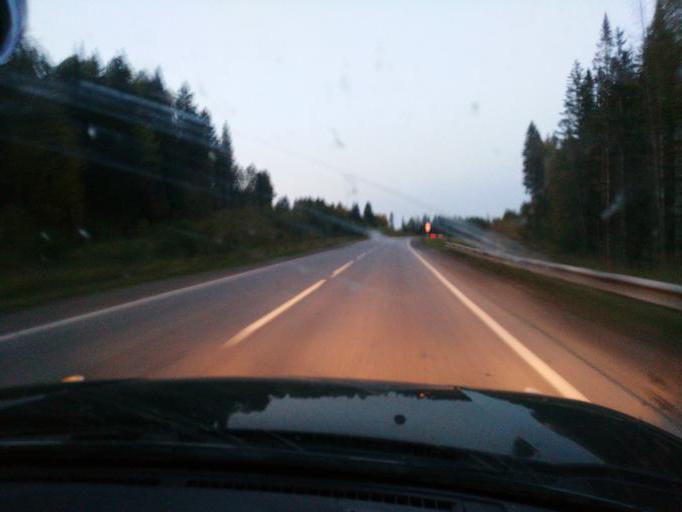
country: RU
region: Perm
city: Kalino
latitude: 58.2776
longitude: 57.3968
